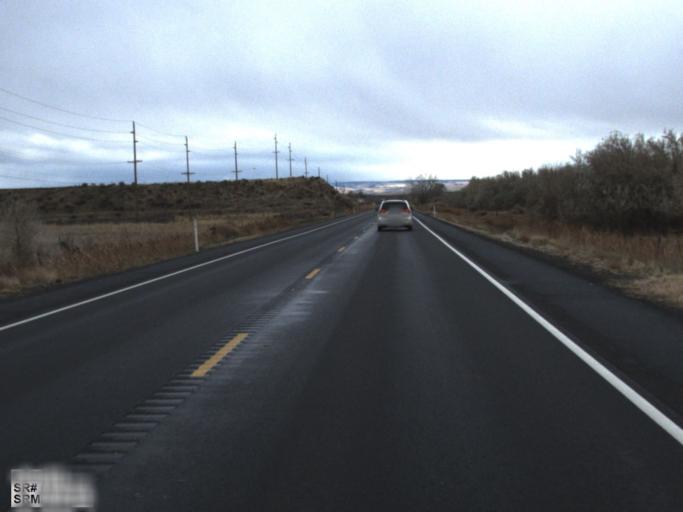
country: US
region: Washington
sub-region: Walla Walla County
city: Garrett
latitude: 46.0461
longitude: -118.6965
